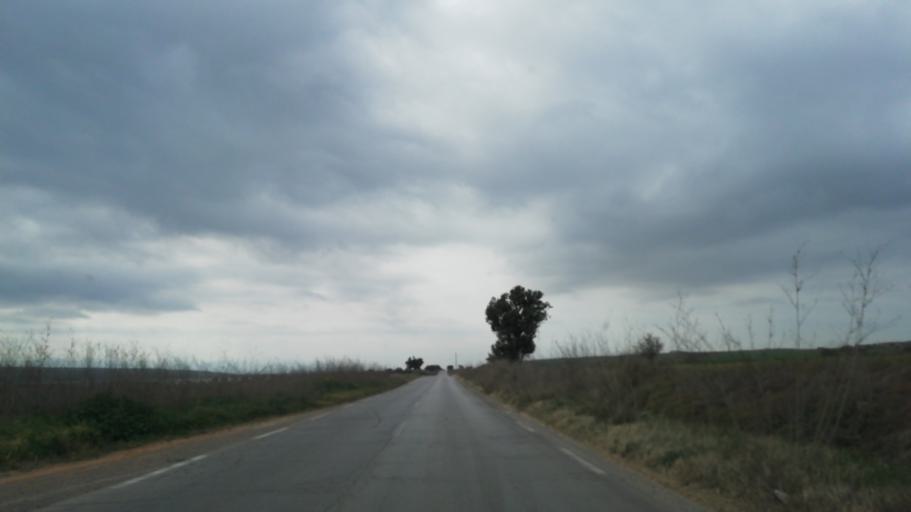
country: DZ
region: Oran
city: Sidi ech Chahmi
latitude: 35.6202
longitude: -0.4129
